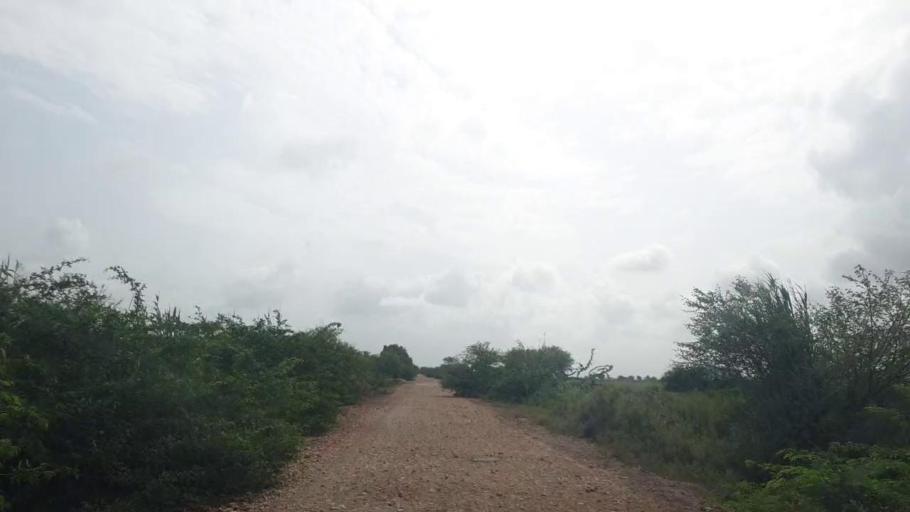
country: PK
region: Sindh
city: Tando Bago
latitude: 24.8195
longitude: 69.0529
